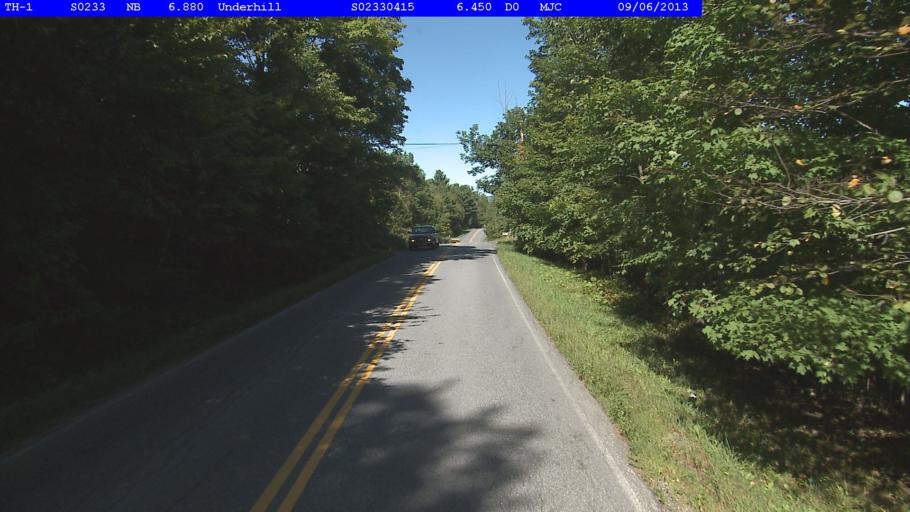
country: US
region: Vermont
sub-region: Chittenden County
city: Jericho
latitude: 44.5579
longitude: -72.8673
